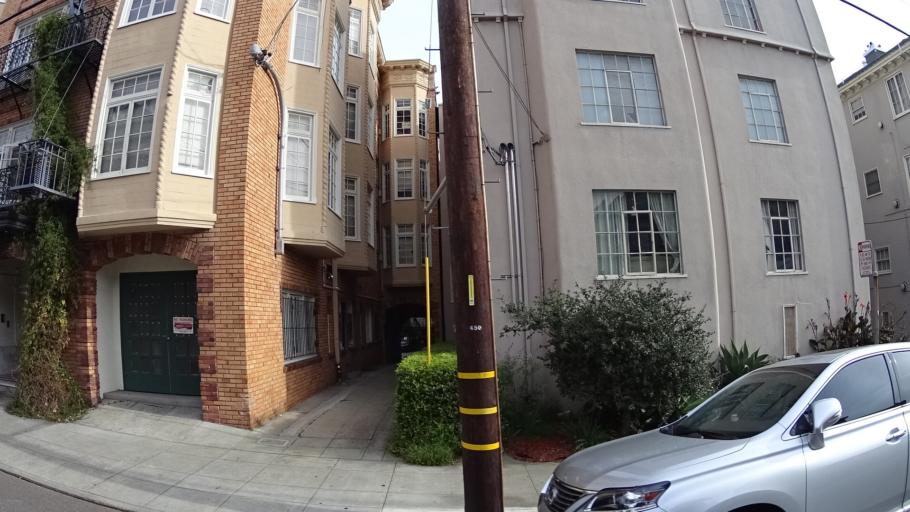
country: US
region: California
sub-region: Alameda County
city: Oakland
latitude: 37.8097
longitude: -122.2570
